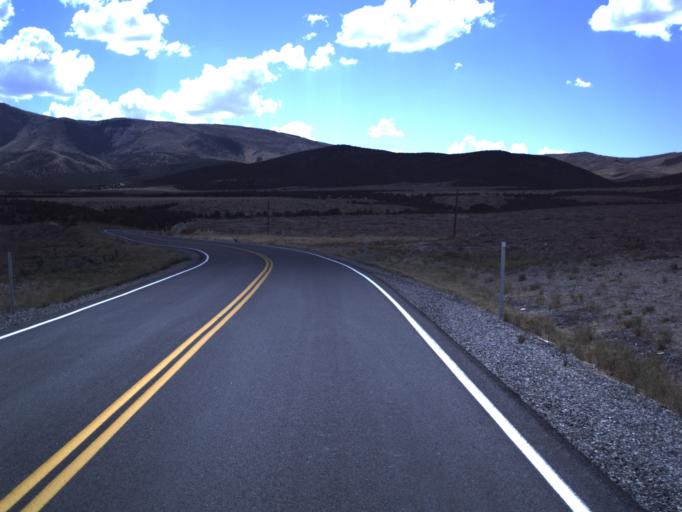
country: US
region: Utah
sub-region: Tooele County
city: Grantsville
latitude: 40.3350
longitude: -112.5087
